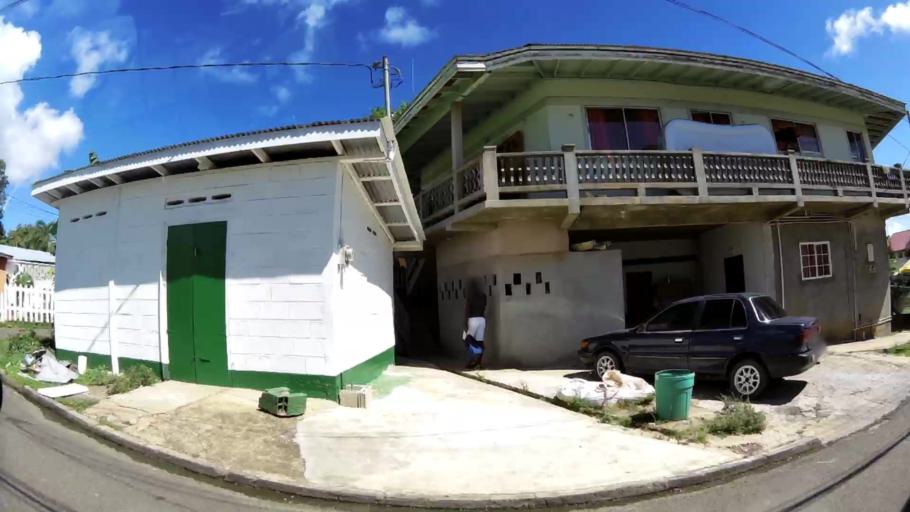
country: TT
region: Tobago
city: Scarborough
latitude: 11.1817
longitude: -60.8076
